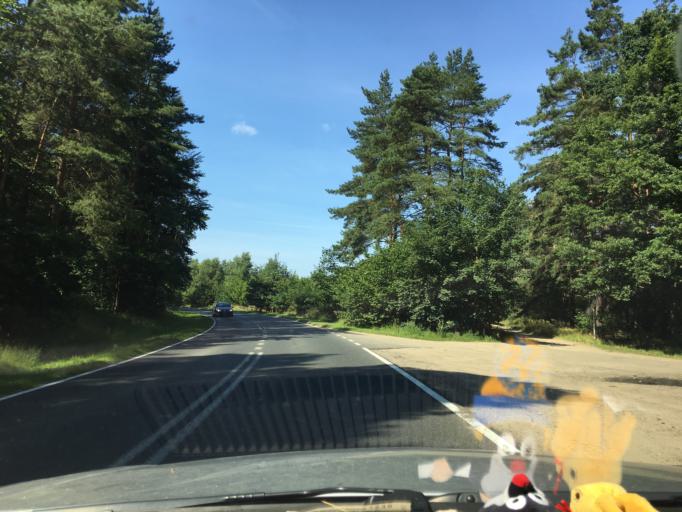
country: PL
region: West Pomeranian Voivodeship
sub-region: Powiat kamienski
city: Wolin
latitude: 53.9721
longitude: 14.5972
